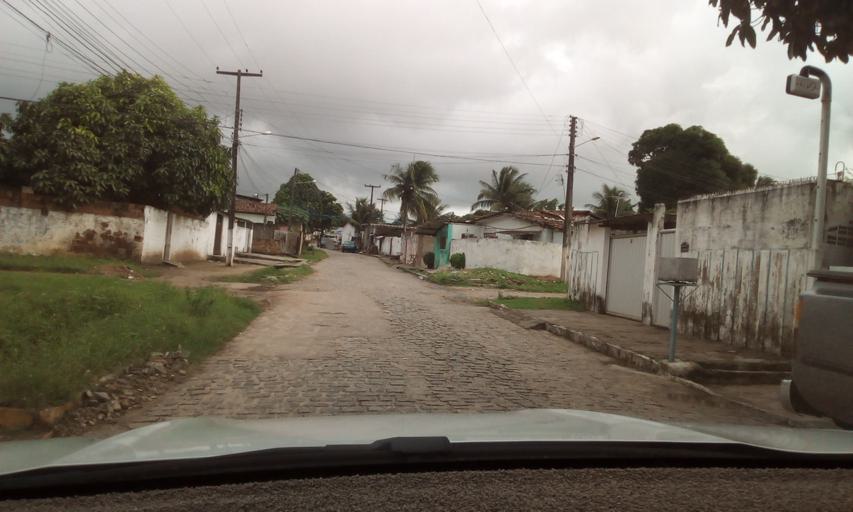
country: BR
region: Paraiba
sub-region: Bayeux
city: Bayeux
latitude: -7.1526
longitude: -34.9030
